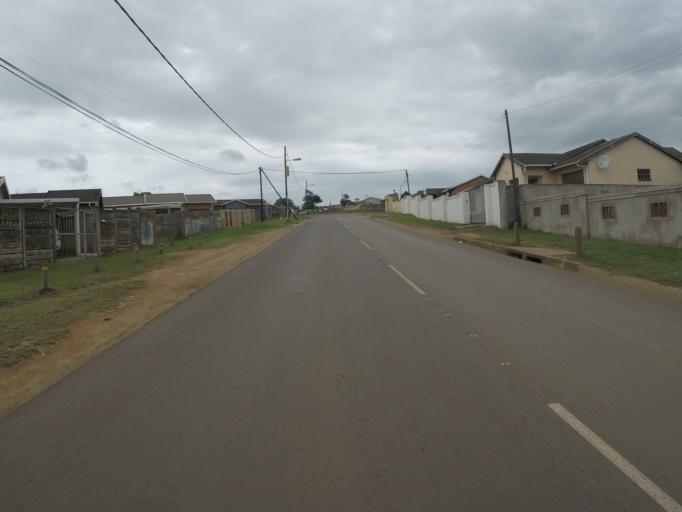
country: ZA
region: KwaZulu-Natal
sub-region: uThungulu District Municipality
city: Empangeni
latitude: -28.7828
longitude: 31.8500
